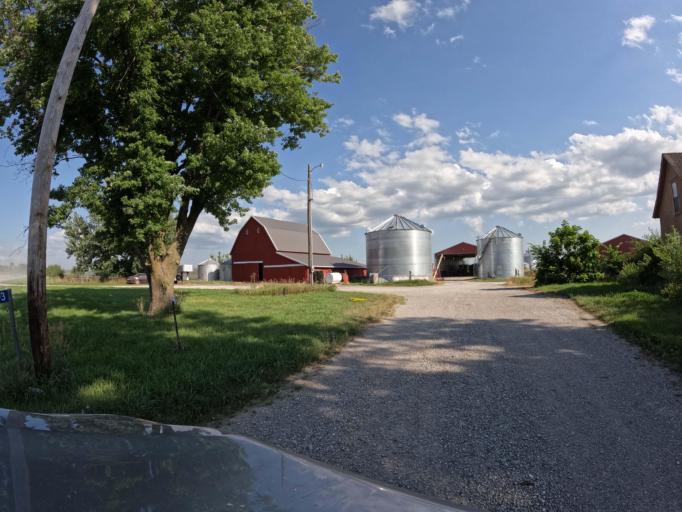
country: US
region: Iowa
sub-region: Appanoose County
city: Centerville
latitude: 40.7177
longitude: -93.0439
